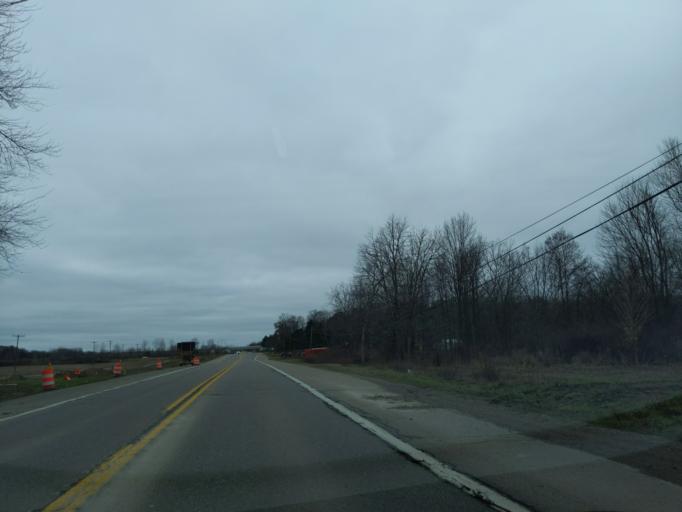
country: US
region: Michigan
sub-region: Clinton County
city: Saint Johns
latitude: 43.0013
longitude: -84.5098
